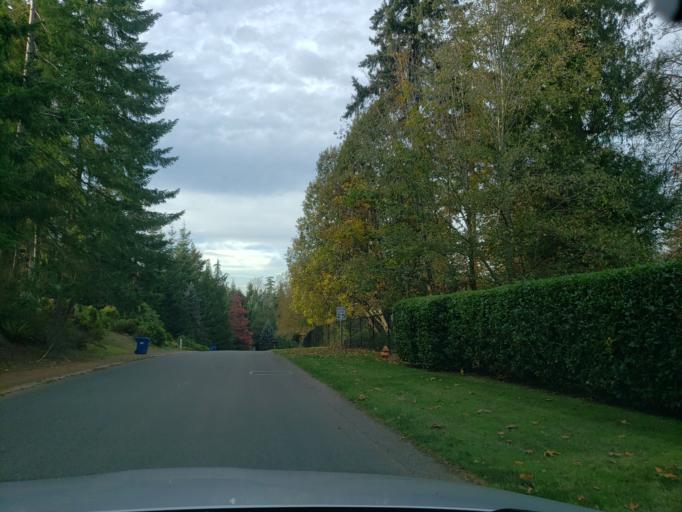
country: US
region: Washington
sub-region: Snohomish County
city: Woodway
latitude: 47.7971
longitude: -122.3826
